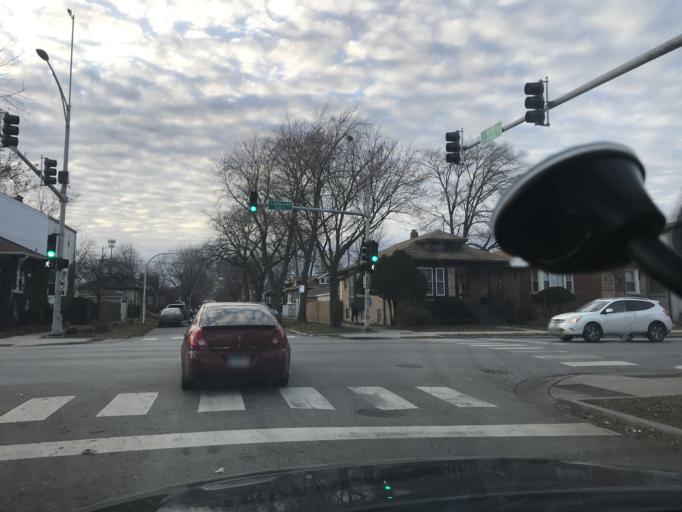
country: US
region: Indiana
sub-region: Lake County
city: Whiting
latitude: 41.7480
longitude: -87.5757
